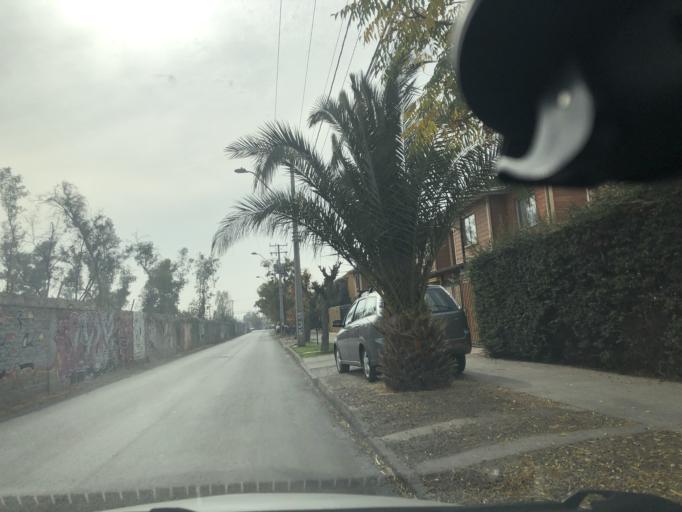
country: CL
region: Santiago Metropolitan
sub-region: Provincia de Cordillera
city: Puente Alto
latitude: -33.5782
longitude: -70.5763
